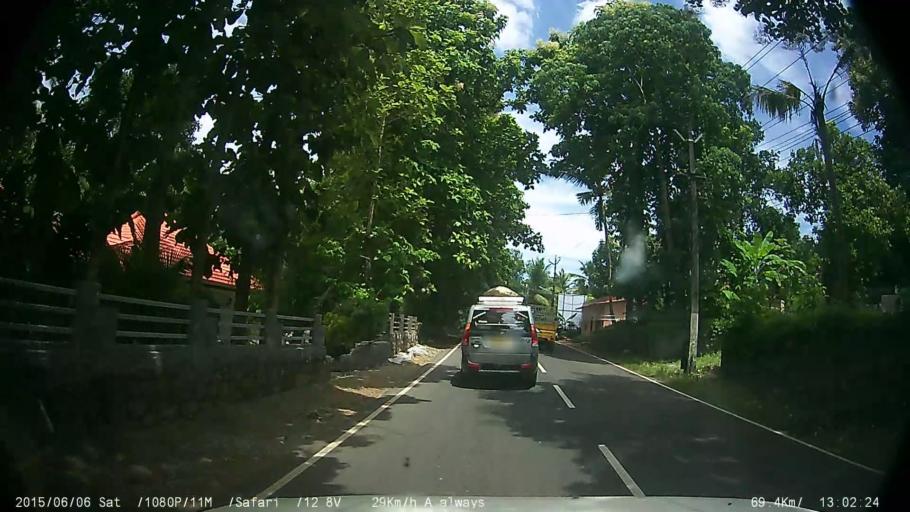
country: IN
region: Kerala
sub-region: Kottayam
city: Changanacheri
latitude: 9.4665
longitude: 76.5786
